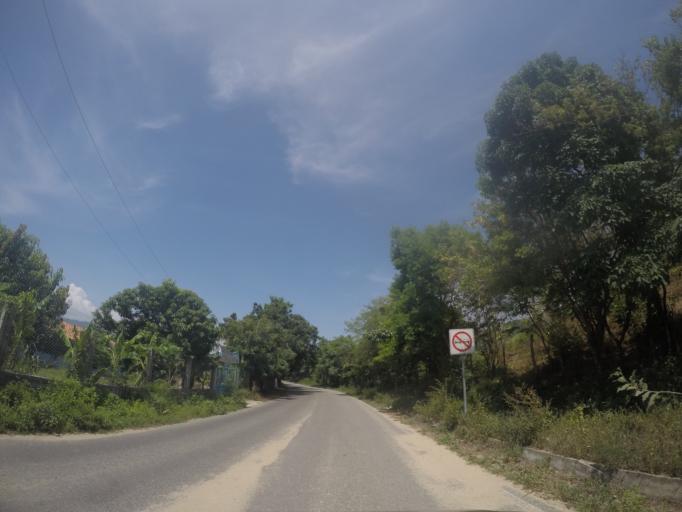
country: MX
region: Oaxaca
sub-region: Villa de Tututepec de Melchor Ocampo
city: Santa Rosa de Lima
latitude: 15.9882
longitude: -97.5457
